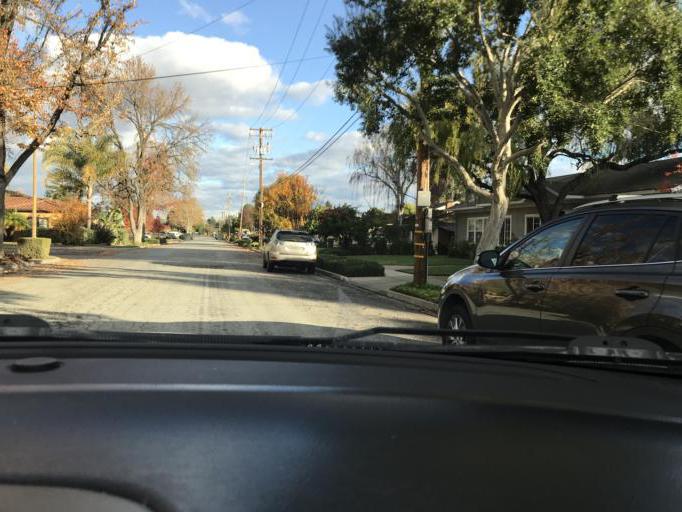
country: US
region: California
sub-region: Santa Clara County
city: Campbell
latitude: 37.2915
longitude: -121.9203
